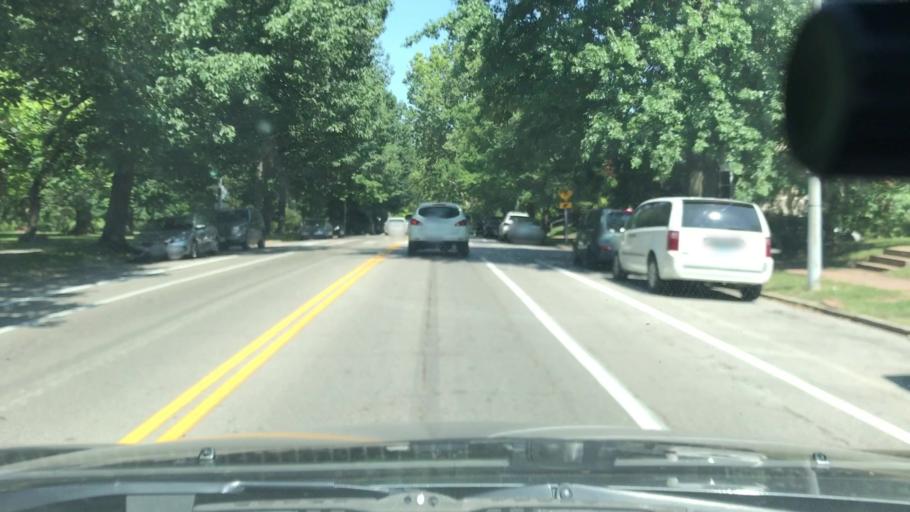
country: US
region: Missouri
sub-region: Saint Louis County
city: Richmond Heights
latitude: 38.6051
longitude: -90.2661
